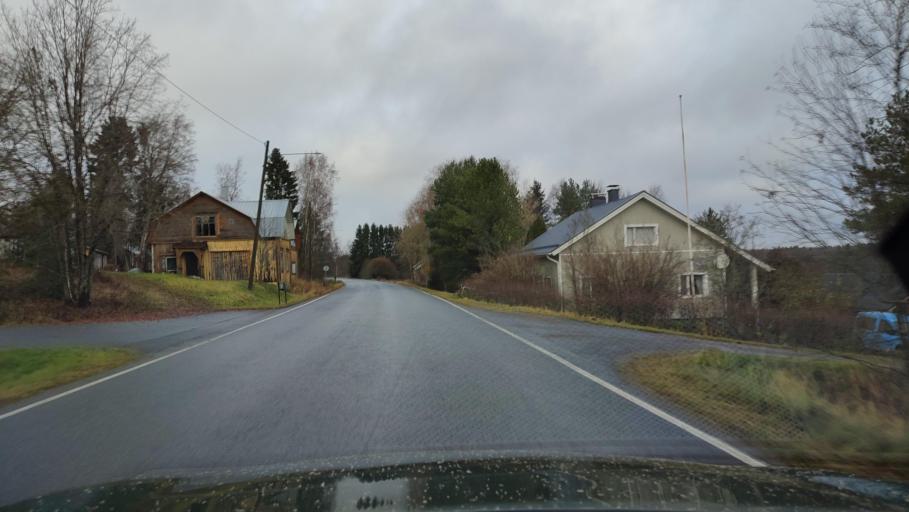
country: FI
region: Southern Ostrobothnia
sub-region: Suupohja
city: Karijoki
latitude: 62.3824
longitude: 21.5580
